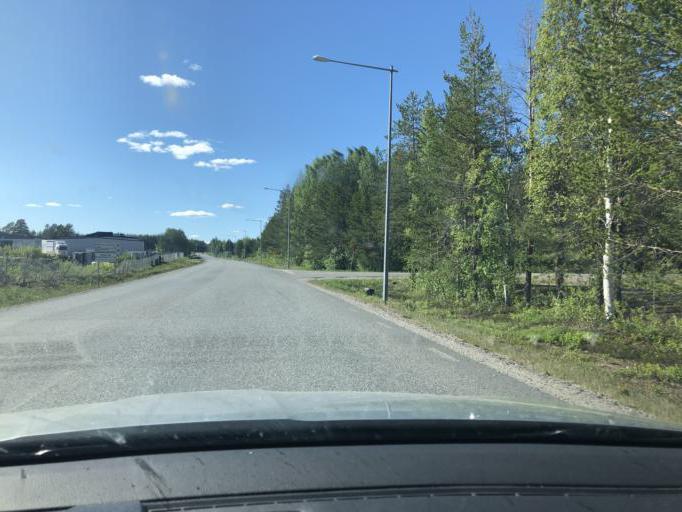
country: SE
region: Norrbotten
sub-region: Kalix Kommun
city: Kalix
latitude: 65.8570
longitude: 23.1747
